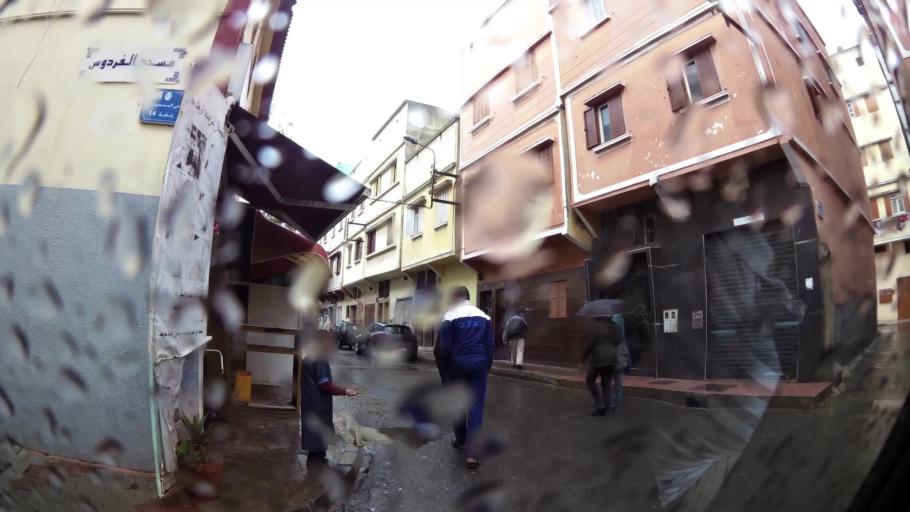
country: MA
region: Grand Casablanca
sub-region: Casablanca
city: Casablanca
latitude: 33.5456
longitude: -7.5784
